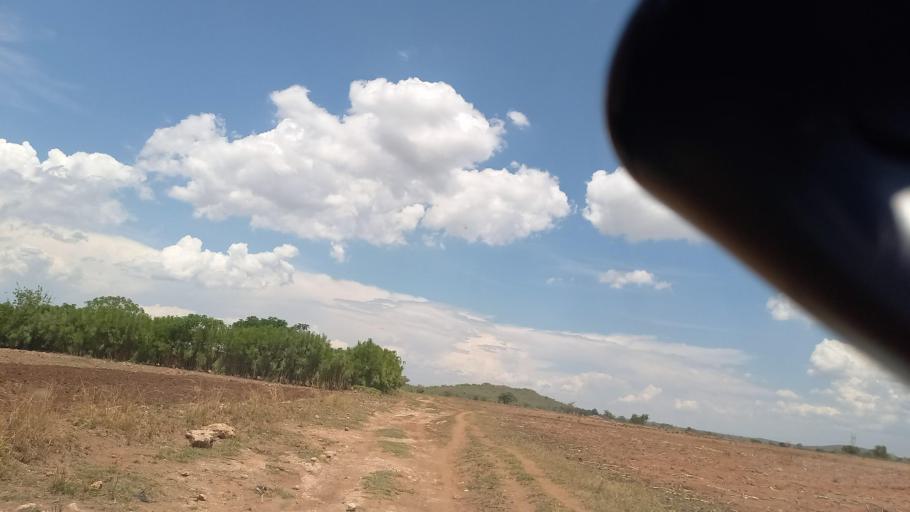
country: ZM
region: Southern
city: Mazabuka
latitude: -16.1102
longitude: 27.8257
